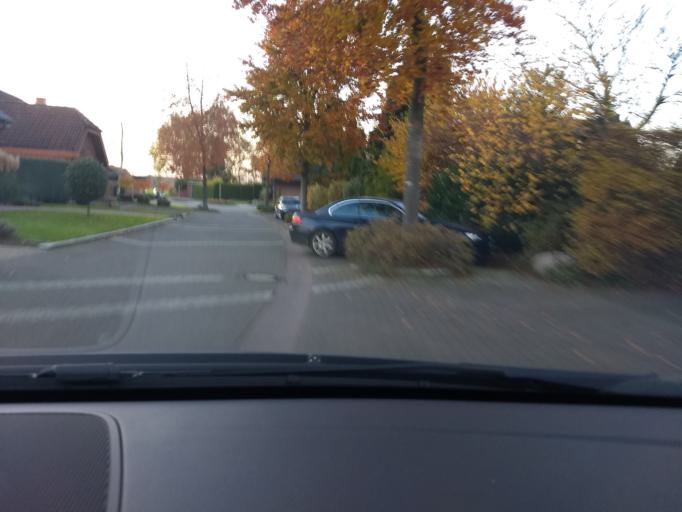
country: DE
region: North Rhine-Westphalia
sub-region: Regierungsbezirk Munster
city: Heiden
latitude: 51.8291
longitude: 6.9250
